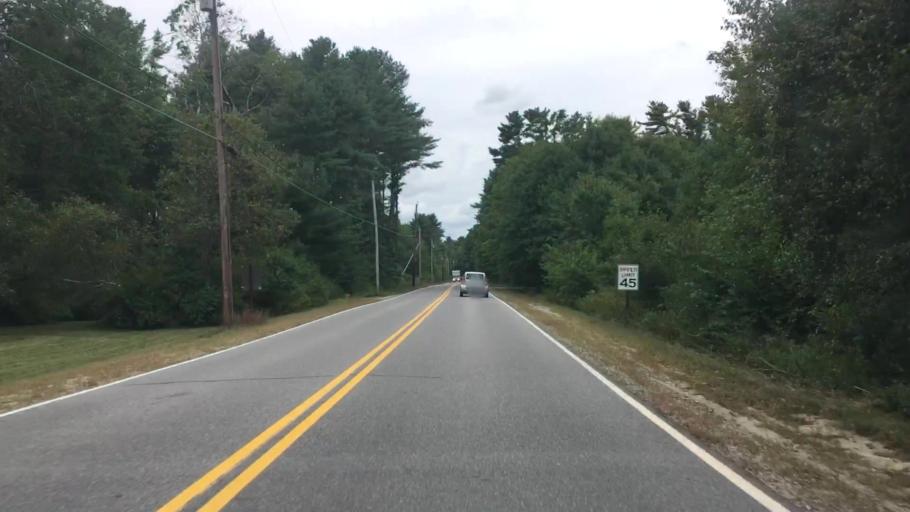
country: US
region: Maine
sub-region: Cumberland County
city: Cumberland Center
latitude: 43.8688
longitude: -70.2289
